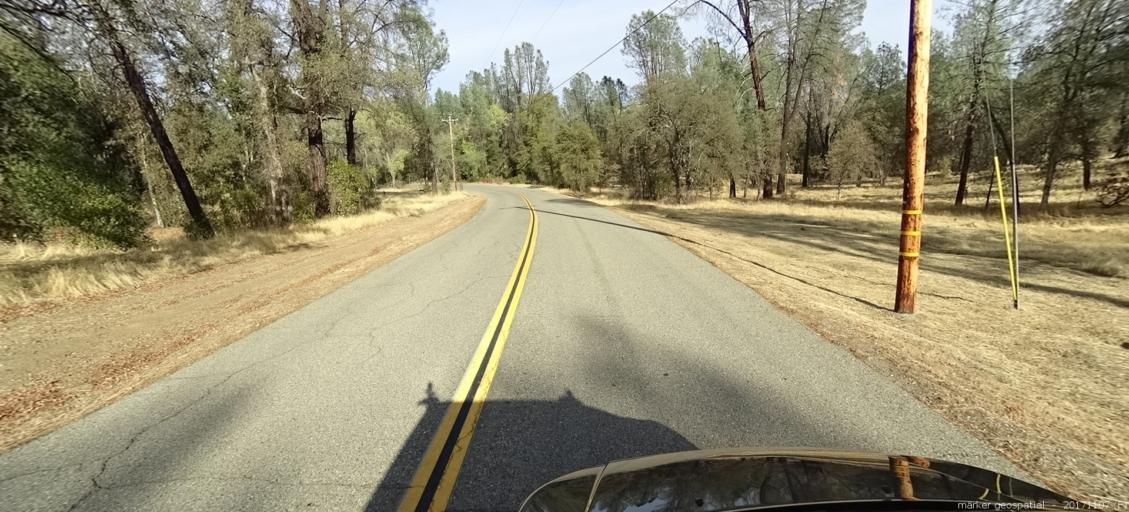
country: US
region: California
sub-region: Shasta County
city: Redding
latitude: 40.5117
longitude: -122.4418
